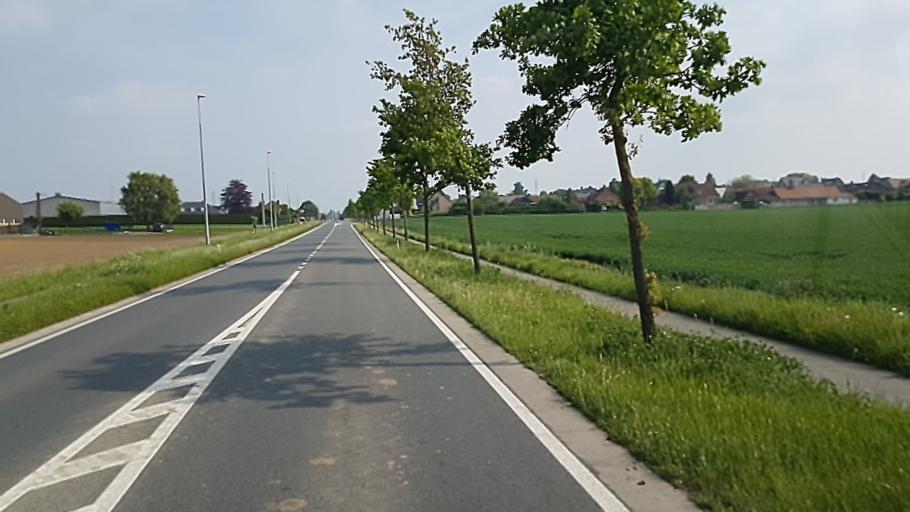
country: BE
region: Flanders
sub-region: Provincie West-Vlaanderen
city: Zwevegem
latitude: 50.7874
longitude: 3.2956
